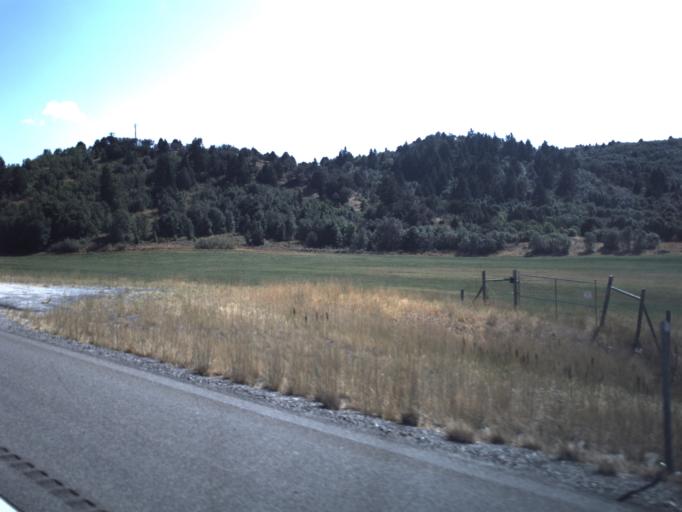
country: US
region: Utah
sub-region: Box Elder County
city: Brigham City
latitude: 41.5541
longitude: -111.9561
